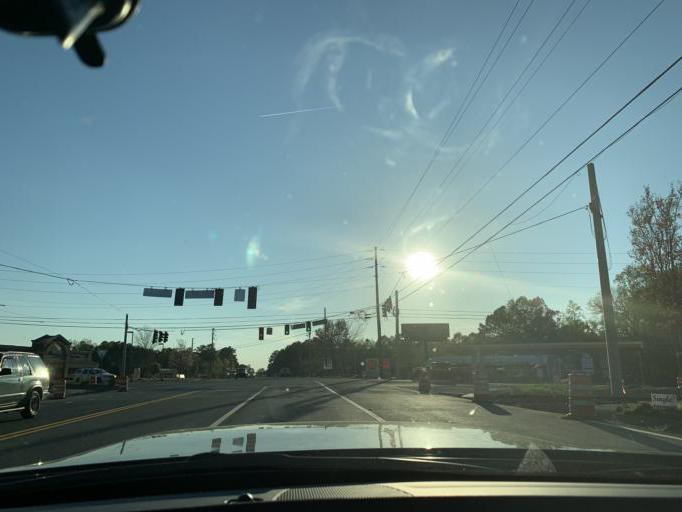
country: US
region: Georgia
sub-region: Forsyth County
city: Cumming
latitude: 34.2395
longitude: -84.1941
